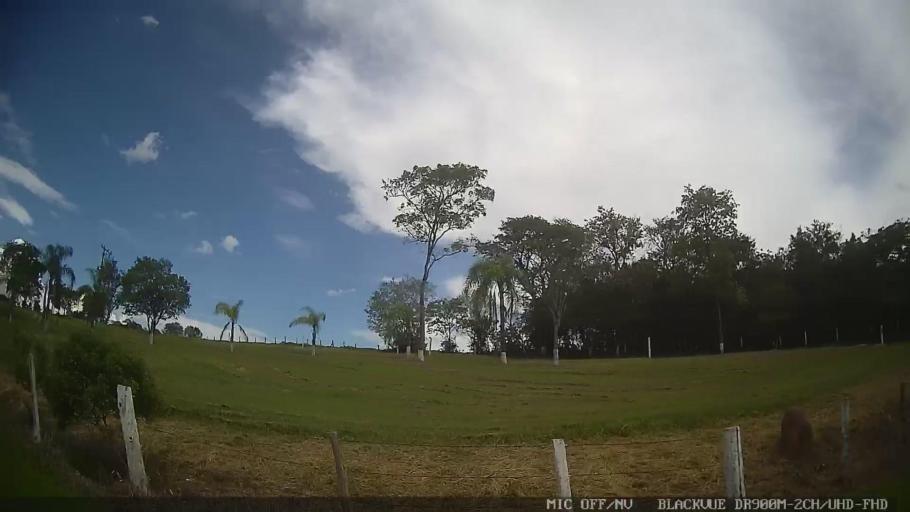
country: BR
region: Sao Paulo
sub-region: Conchas
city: Conchas
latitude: -22.9887
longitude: -47.9944
